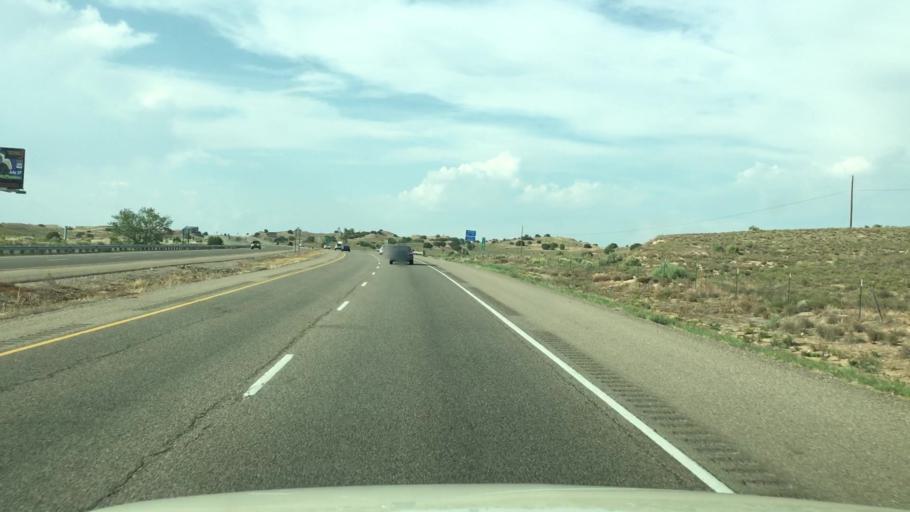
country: US
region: New Mexico
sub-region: Santa Fe County
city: Pojoaque
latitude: 35.9135
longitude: -106.0166
